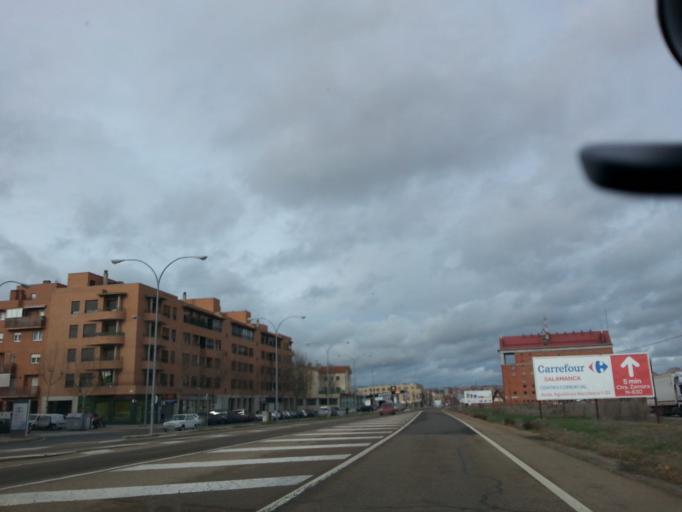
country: ES
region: Castille and Leon
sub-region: Provincia de Salamanca
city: Carbajosa de la Sagrada
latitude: 40.9456
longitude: -5.6695
